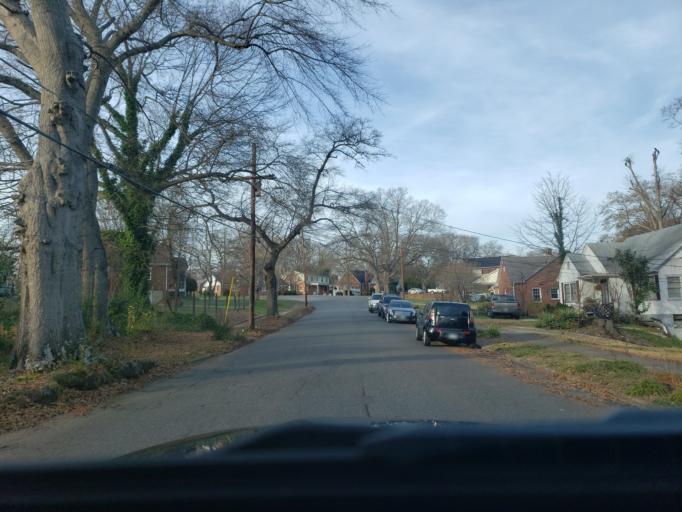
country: US
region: North Carolina
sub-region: Cleveland County
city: Shelby
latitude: 35.2867
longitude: -81.5283
